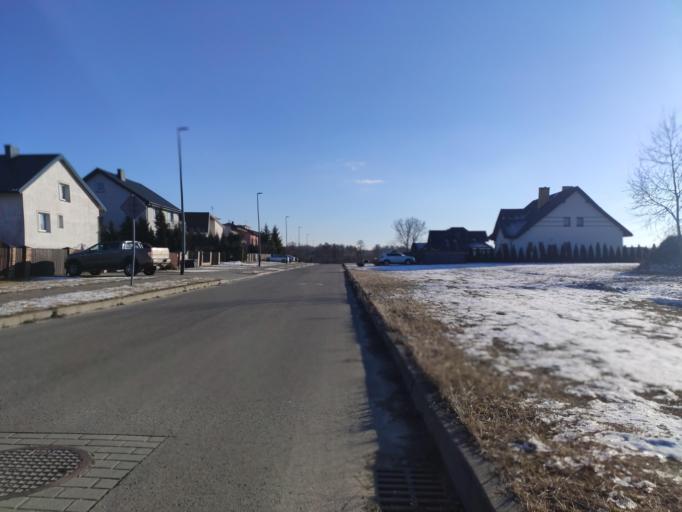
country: PL
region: Lublin Voivodeship
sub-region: Powiat lubartowski
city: Kock
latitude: 51.6406
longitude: 22.4295
